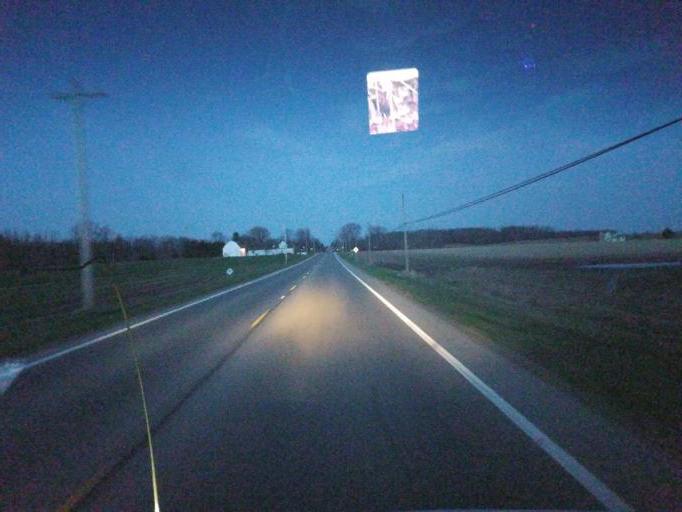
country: US
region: Ohio
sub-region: Logan County
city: De Graff
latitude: 40.3669
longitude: -83.8537
